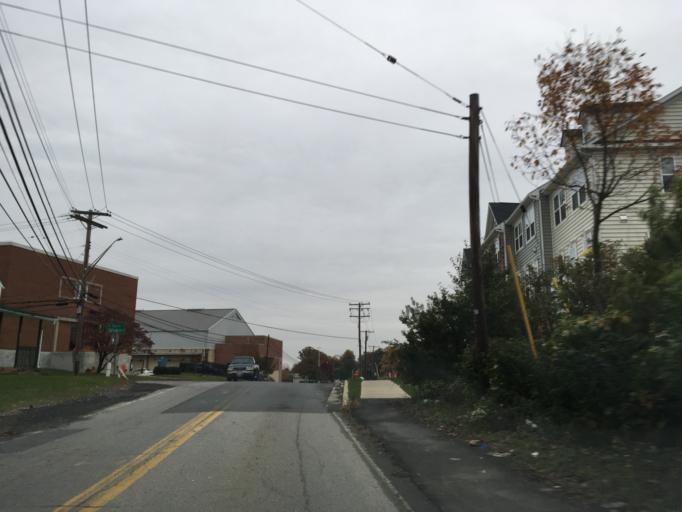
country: US
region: Maryland
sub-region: Baltimore County
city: Catonsville
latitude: 39.2890
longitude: -76.7215
